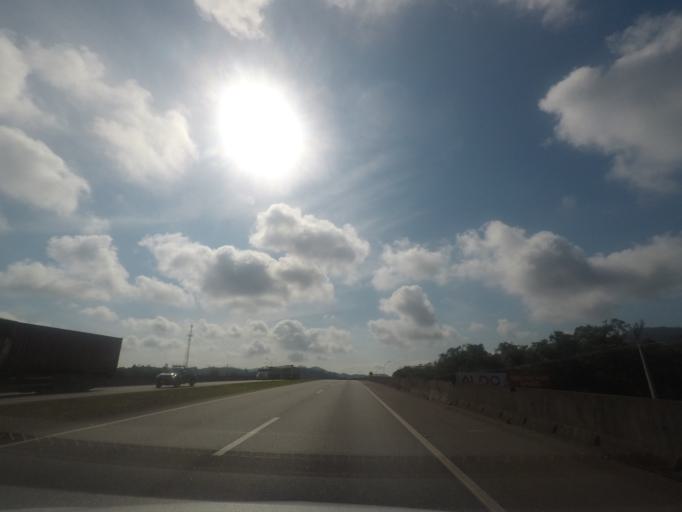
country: BR
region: Parana
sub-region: Antonina
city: Antonina
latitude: -25.5487
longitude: -48.7929
